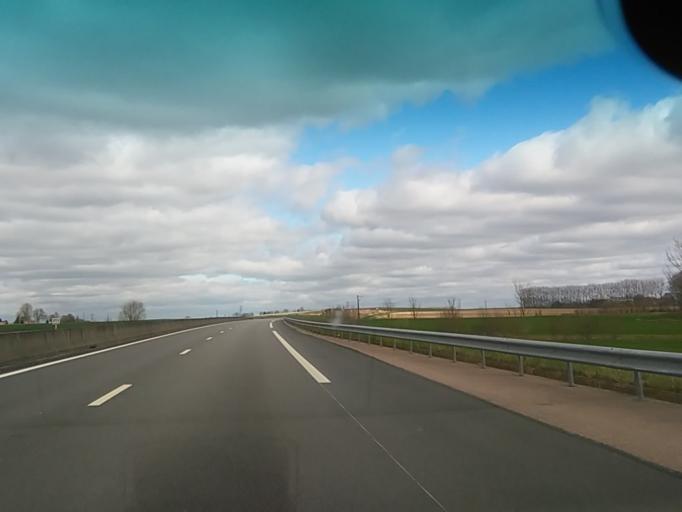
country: FR
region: Haute-Normandie
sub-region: Departement de l'Eure
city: Bourg-Achard
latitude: 49.2965
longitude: 0.7907
